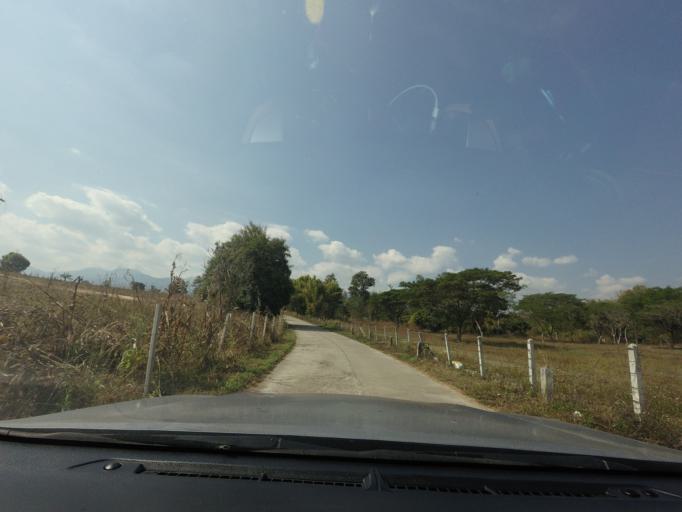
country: TH
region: Mae Hong Son
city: Wiang Nuea
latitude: 19.3844
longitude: 98.4339
